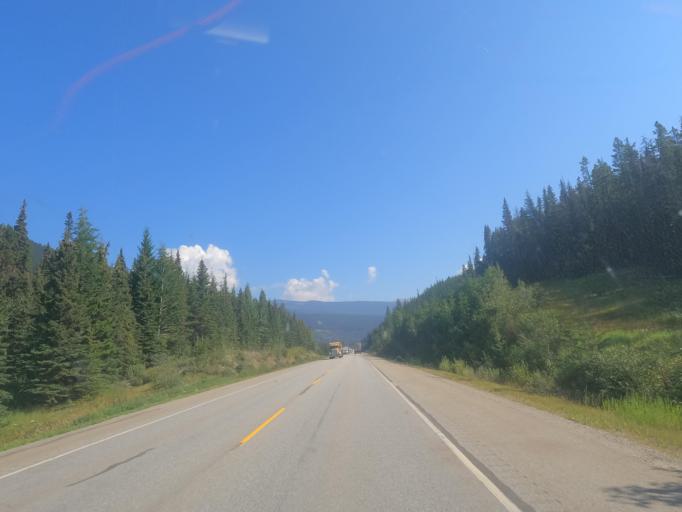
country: CA
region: Alberta
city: Jasper Park Lodge
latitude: 52.8728
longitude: -118.5009
